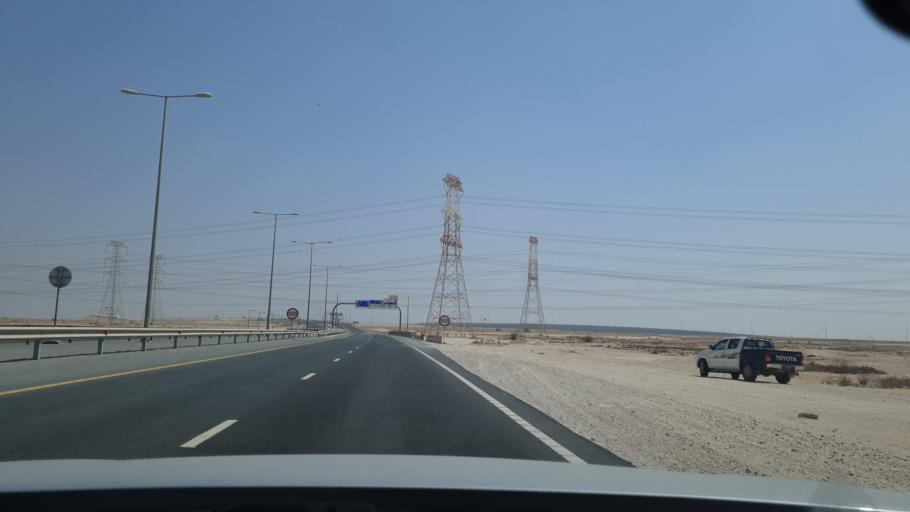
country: QA
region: Baladiyat az Za`ayin
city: Az Za`ayin
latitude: 25.6193
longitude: 51.3527
